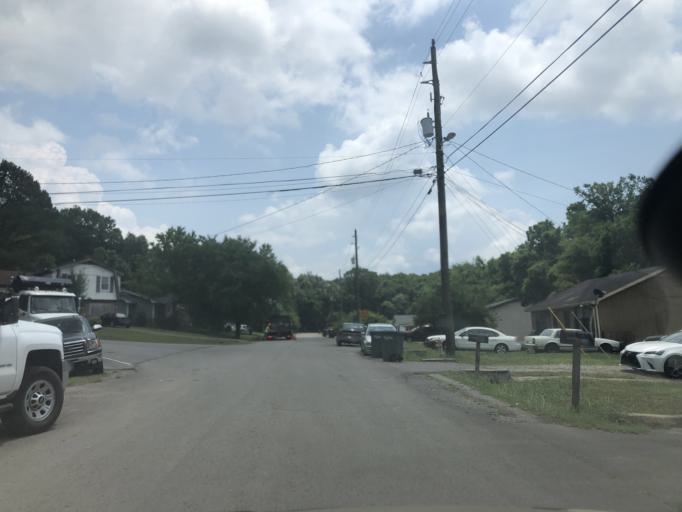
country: US
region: Tennessee
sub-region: Davidson County
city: Lakewood
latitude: 36.2110
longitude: -86.6298
